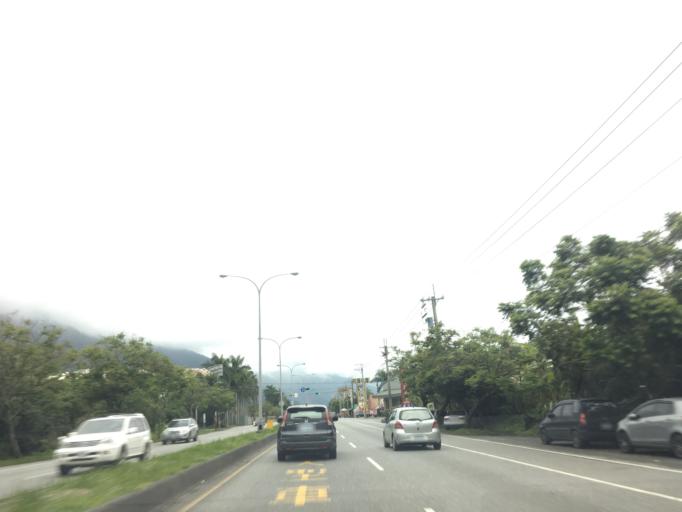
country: TW
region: Taiwan
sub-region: Hualien
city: Hualian
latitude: 24.0474
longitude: 121.6045
